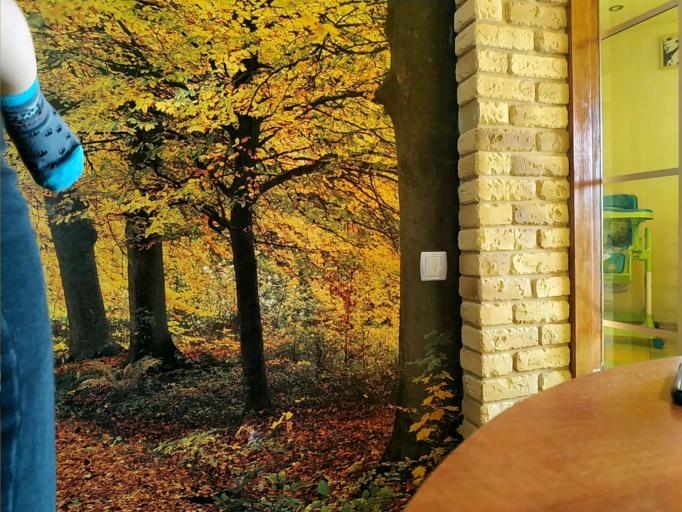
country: RU
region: Novgorod
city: Parfino
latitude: 57.7995
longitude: 31.6161
